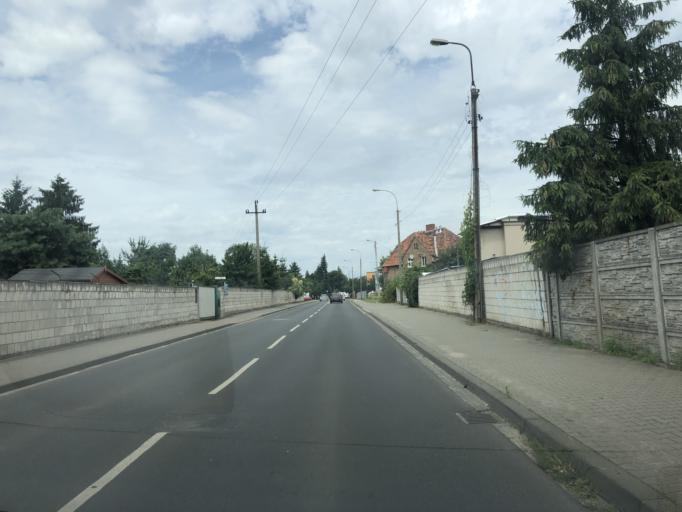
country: PL
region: Greater Poland Voivodeship
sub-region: Powiat poznanski
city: Lubon
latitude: 52.3571
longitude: 16.8838
